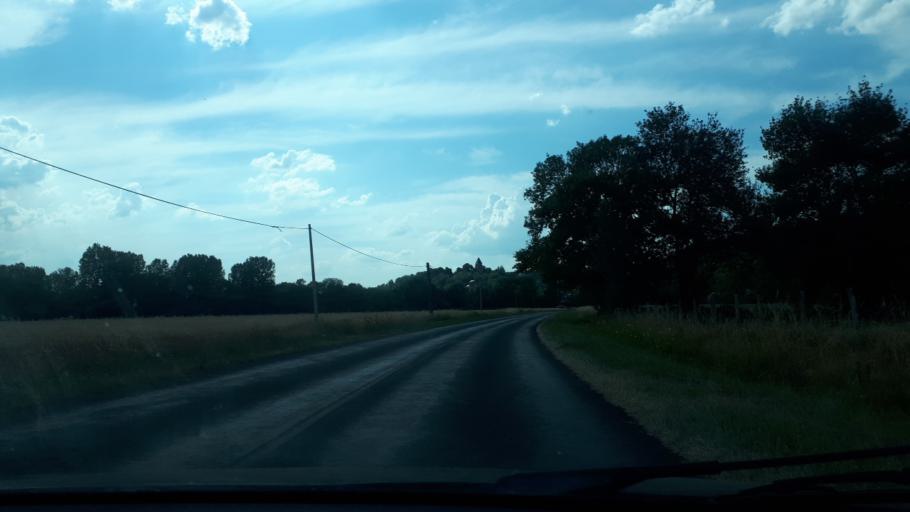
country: FR
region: Centre
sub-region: Departement du Loir-et-Cher
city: Montoire-sur-le-Loir
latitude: 47.7733
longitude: 0.8100
